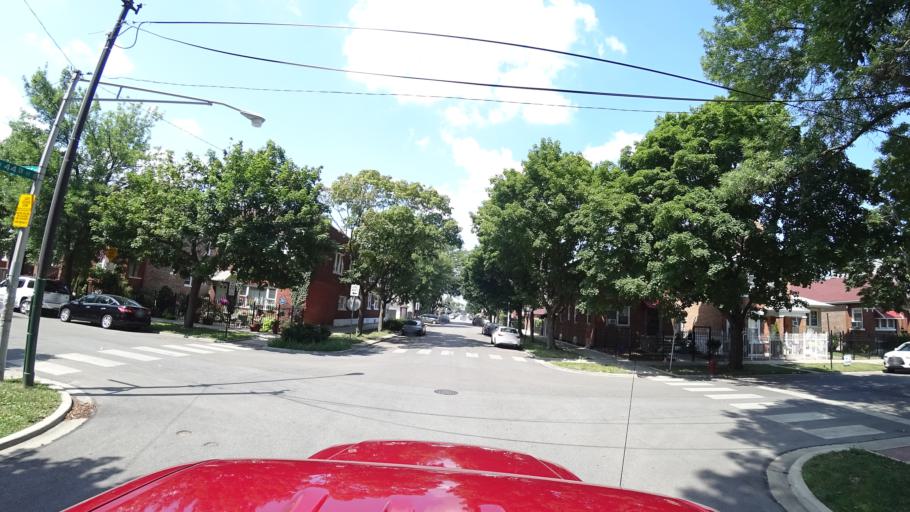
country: US
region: Illinois
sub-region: Cook County
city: Chicago
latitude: 41.8137
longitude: -87.7003
